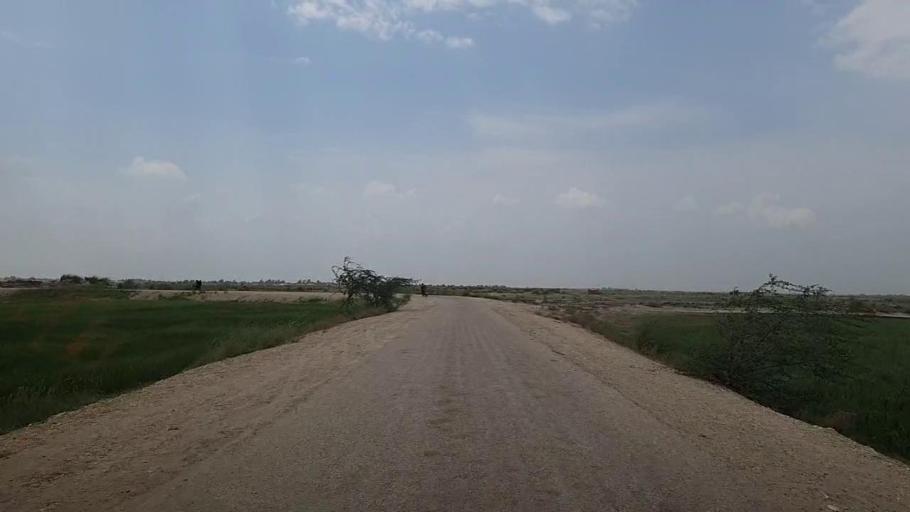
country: PK
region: Sindh
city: Kandhkot
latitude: 28.2936
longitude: 69.1396
